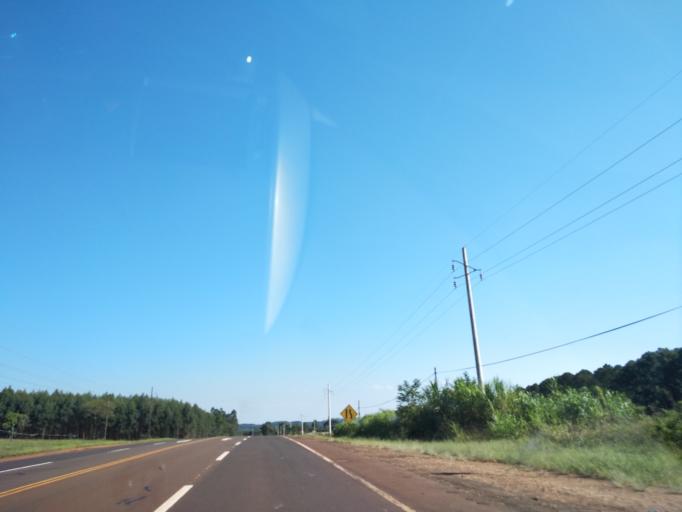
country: AR
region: Misiones
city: Puerto Rico
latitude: -26.8441
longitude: -55.0414
